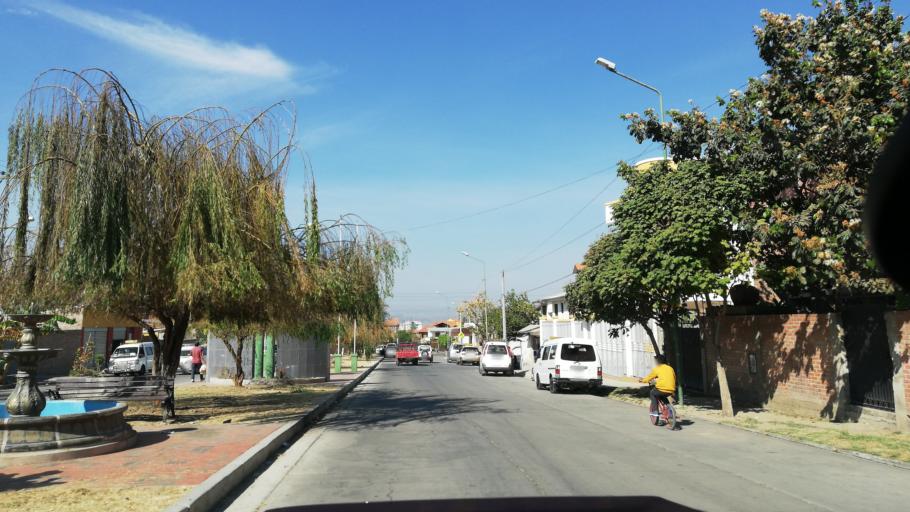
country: BO
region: Cochabamba
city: Cochabamba
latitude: -17.3592
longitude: -66.1863
